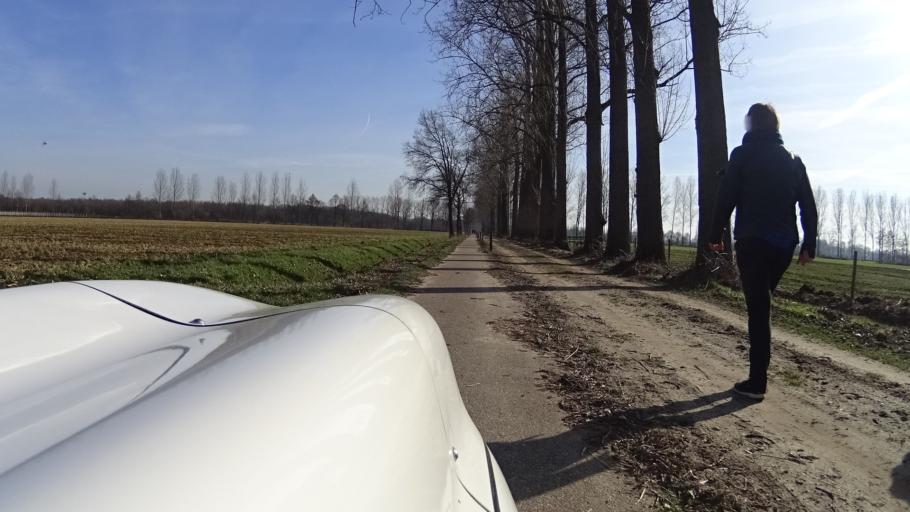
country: NL
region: North Brabant
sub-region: Gemeente Veghel
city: Mariaheide
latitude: 51.6175
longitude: 5.5701
